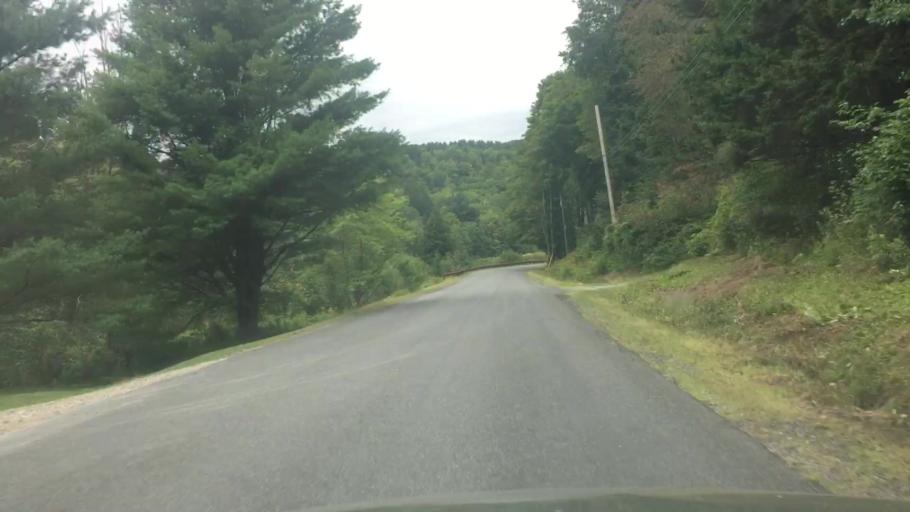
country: US
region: Vermont
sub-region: Windham County
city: Dover
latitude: 42.8484
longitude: -72.8360
